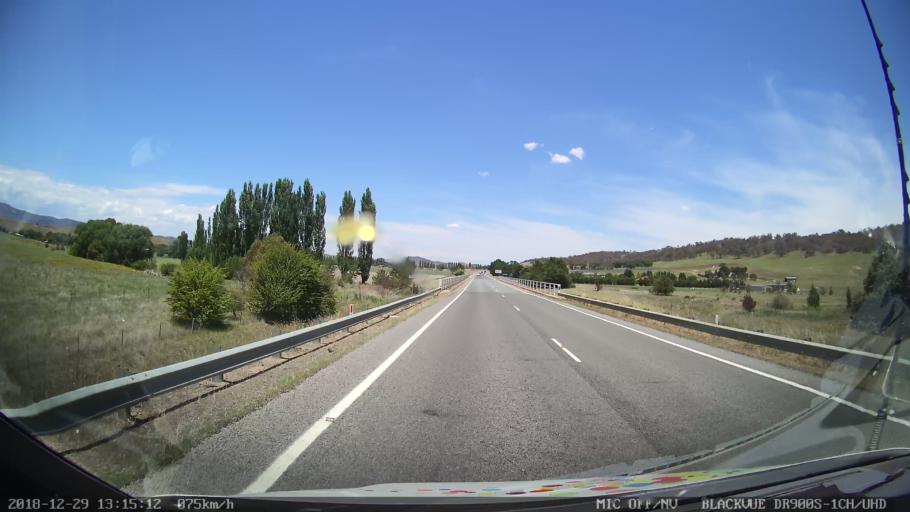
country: AU
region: Australian Capital Territory
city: Macarthur
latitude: -35.7059
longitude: 149.1583
